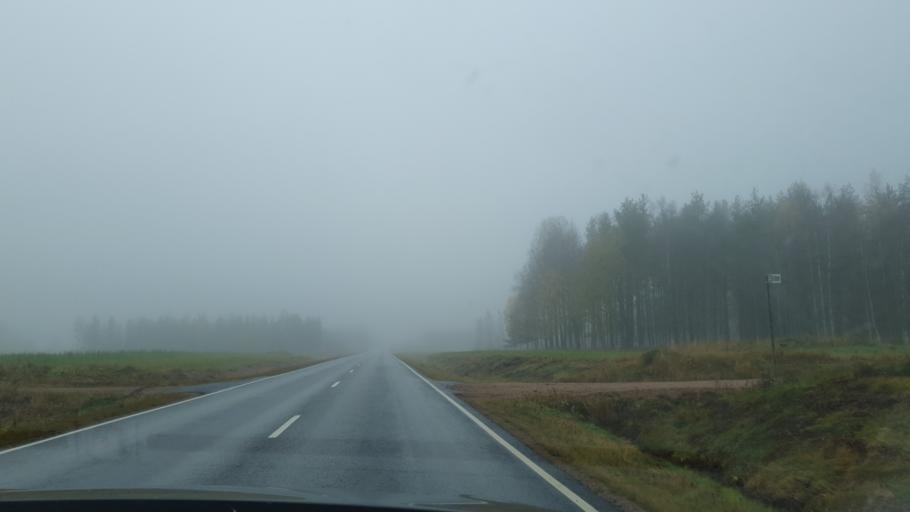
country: FI
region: Lapland
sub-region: Rovaniemi
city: Rovaniemi
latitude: 66.8004
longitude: 25.4140
